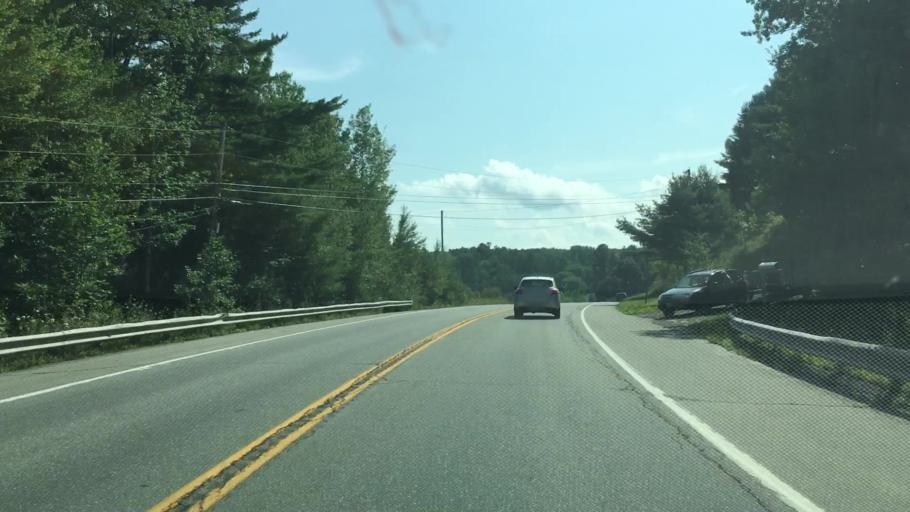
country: US
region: Maine
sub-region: Penobscot County
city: Orrington
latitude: 44.6985
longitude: -68.8448
